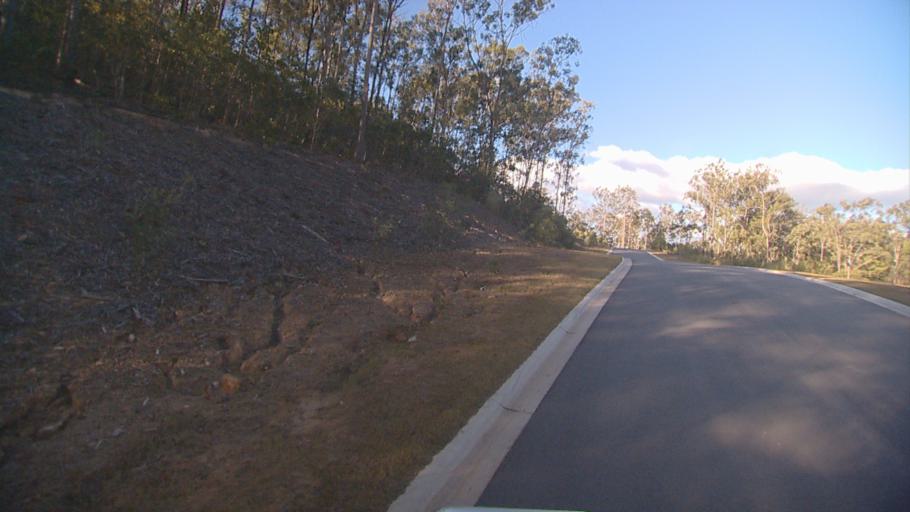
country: AU
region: Queensland
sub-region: Logan
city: Cedar Vale
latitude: -27.9275
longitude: 153.0511
